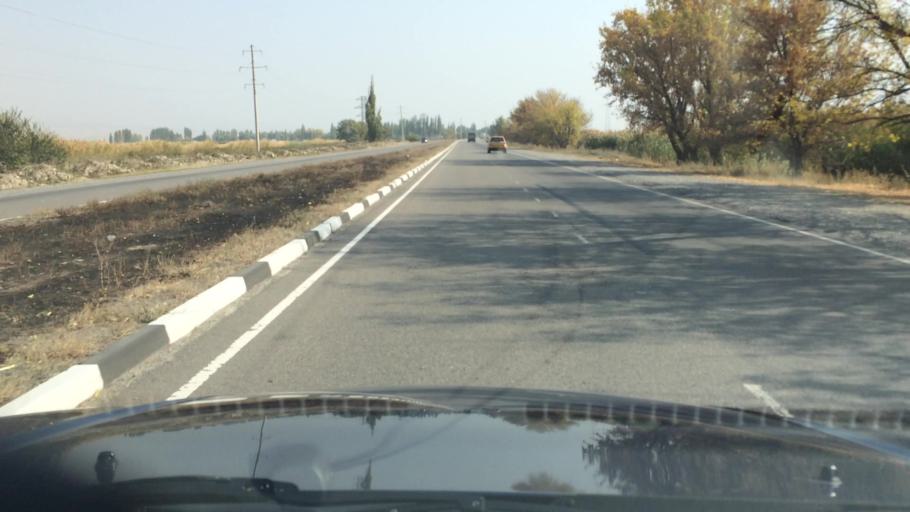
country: KG
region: Chuy
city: Kant
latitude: 42.9658
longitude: 74.8204
